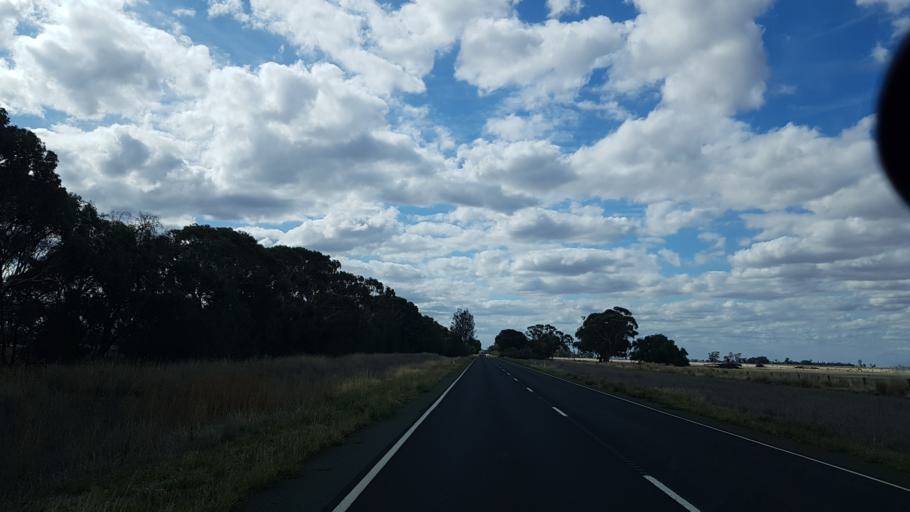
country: AU
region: Victoria
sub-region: Swan Hill
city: Swan Hill
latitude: -35.9836
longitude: 143.9453
